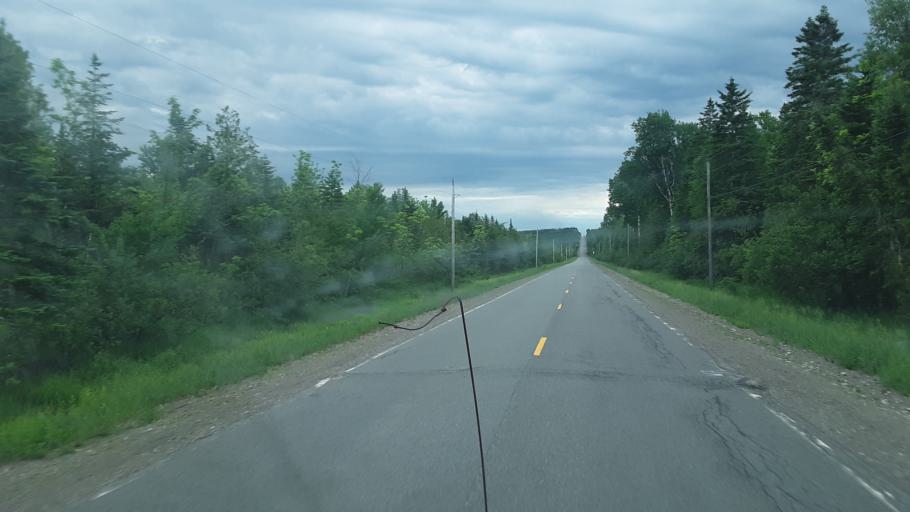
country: US
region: Maine
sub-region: Penobscot County
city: Patten
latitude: 45.8358
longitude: -68.3247
